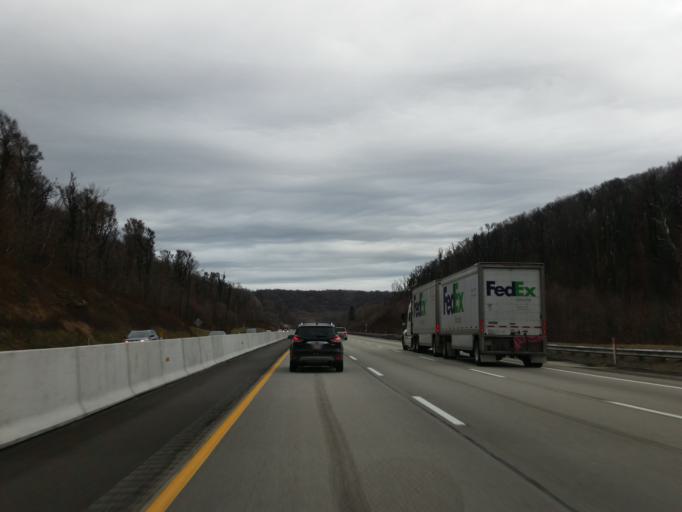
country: US
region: Pennsylvania
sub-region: Westmoreland County
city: Ligonier
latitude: 40.1095
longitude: -79.2450
